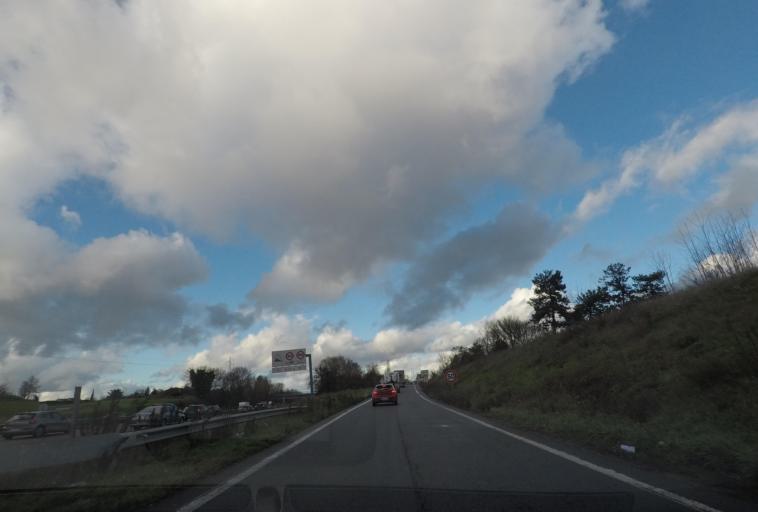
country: FR
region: Ile-de-France
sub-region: Departement de l'Essonne
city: Ormoy
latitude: 48.5701
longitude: 2.4704
